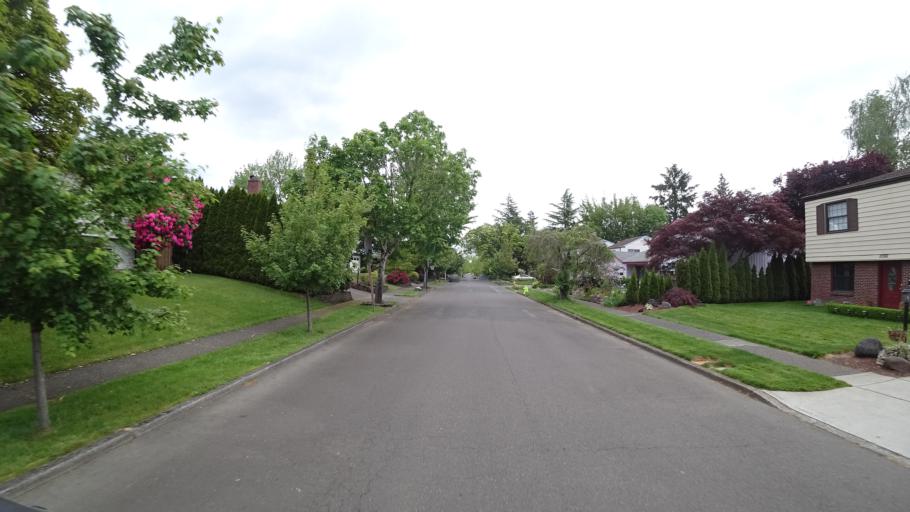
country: US
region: Oregon
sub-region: Washington County
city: Beaverton
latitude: 45.4671
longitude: -122.7982
